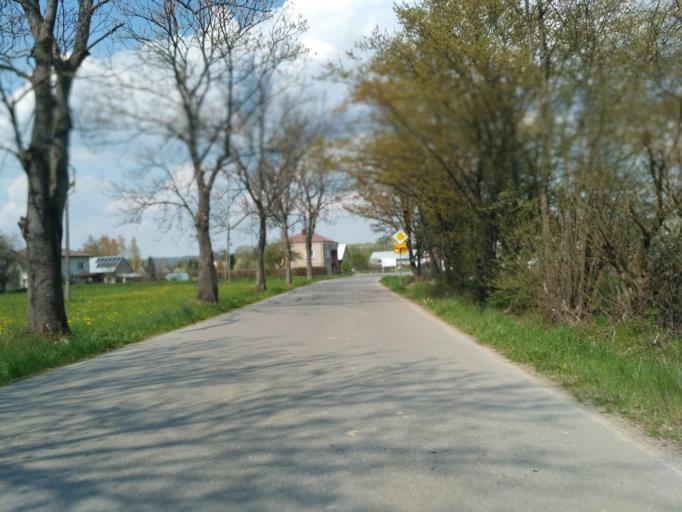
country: PL
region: Subcarpathian Voivodeship
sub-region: Powiat jasielski
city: Tarnowiec
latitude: 49.7436
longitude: 21.5476
